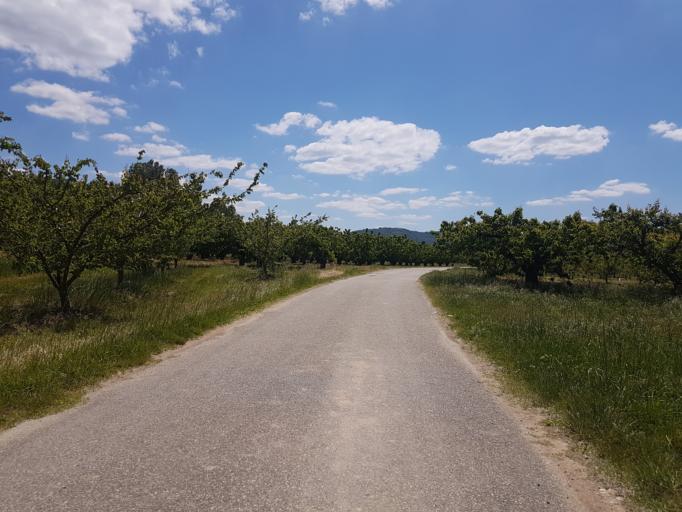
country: FR
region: Rhone-Alpes
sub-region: Departement de l'Ardeche
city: Saint-Jean-de-Muzols
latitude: 45.1008
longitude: 4.8224
